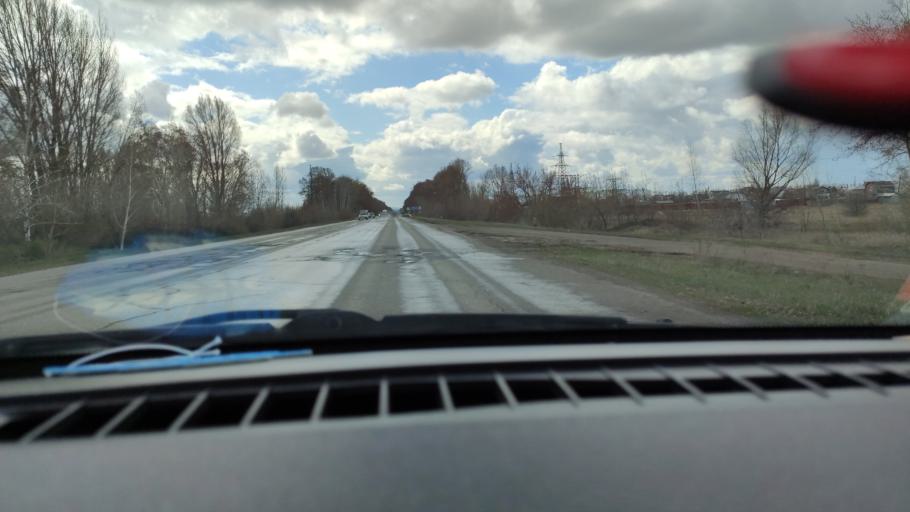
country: RU
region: Samara
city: Tol'yatti
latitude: 53.6293
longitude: 49.4169
